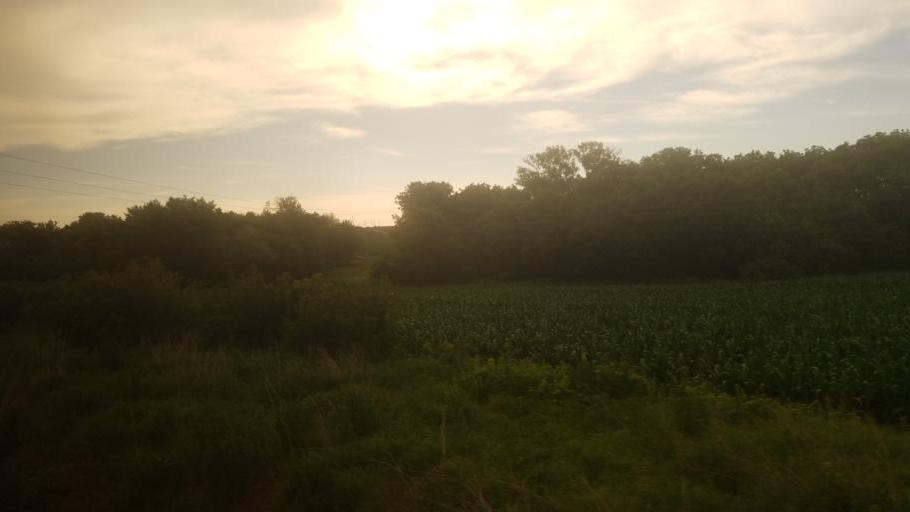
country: US
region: Kansas
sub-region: Osage County
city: Carbondale
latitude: 38.9202
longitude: -95.6955
